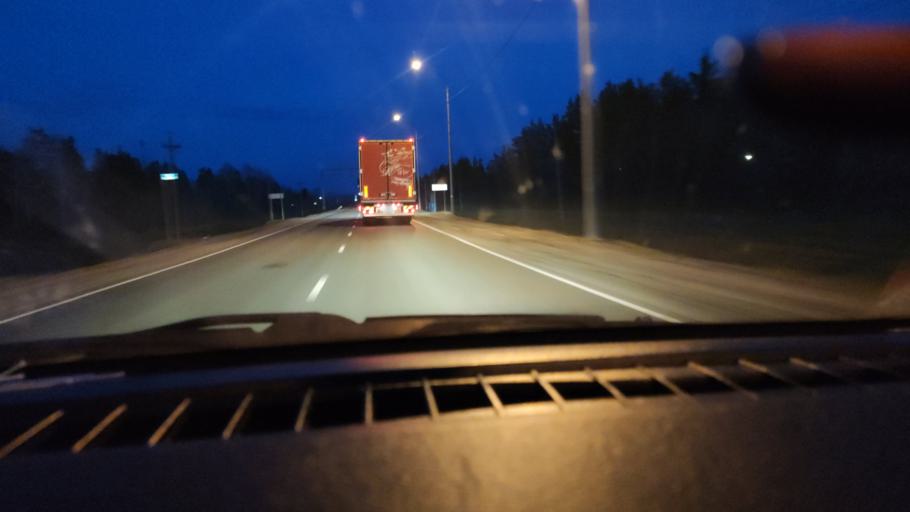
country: RU
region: Saratov
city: Sennoy
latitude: 52.1510
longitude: 46.9736
